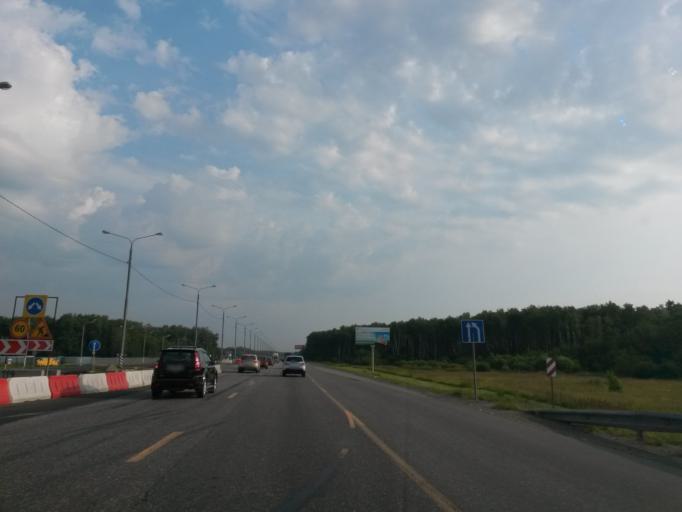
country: RU
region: Moskovskaya
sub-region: Podol'skiy Rayon
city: Podol'sk
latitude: 55.3914
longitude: 37.6053
